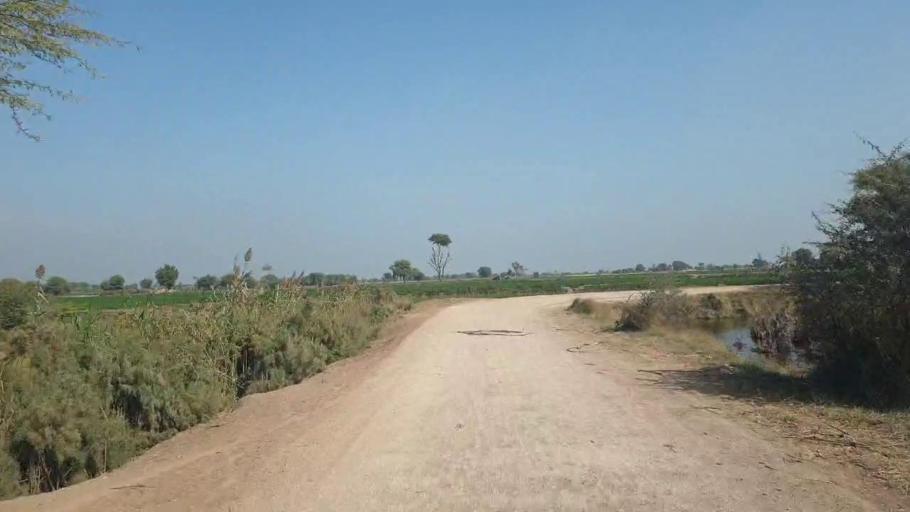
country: PK
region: Sindh
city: Shahdadpur
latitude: 25.9862
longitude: 68.5292
